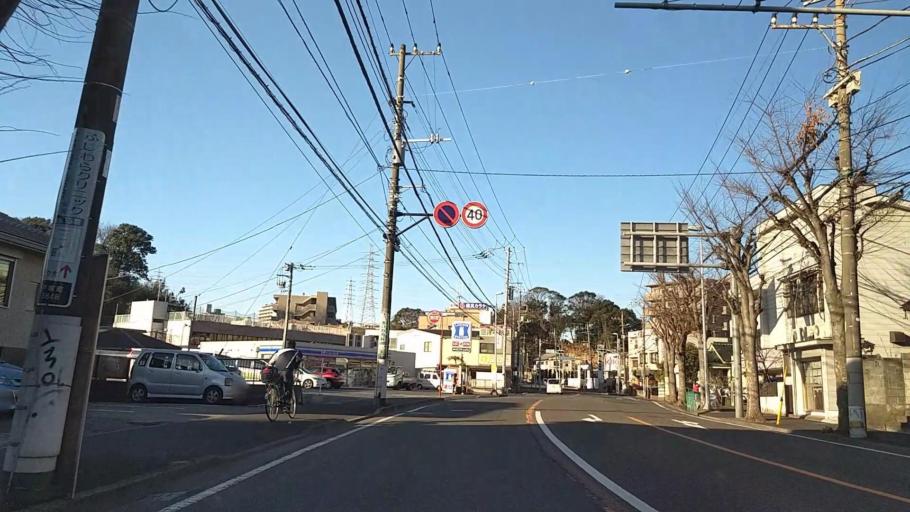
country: JP
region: Kanagawa
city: Fujisawa
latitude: 35.3933
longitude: 139.5283
